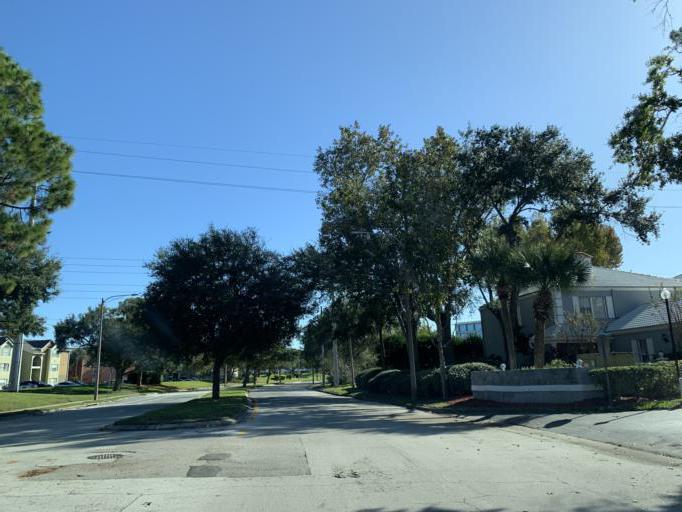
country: US
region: Florida
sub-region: Orange County
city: Oak Ridge
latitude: 28.4891
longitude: -81.4429
